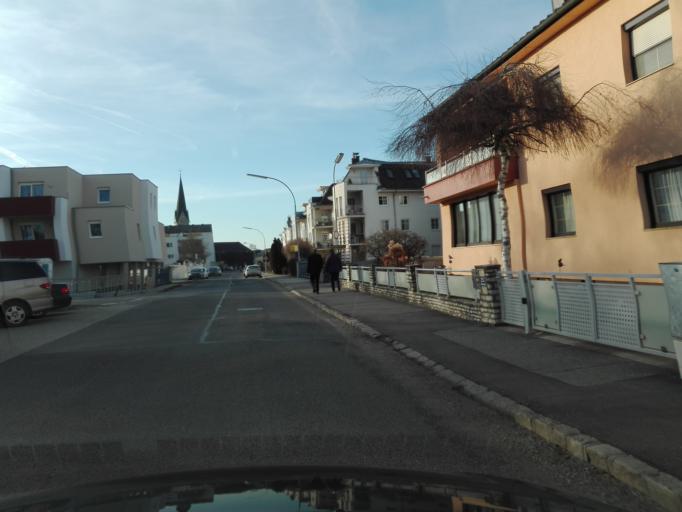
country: AT
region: Lower Austria
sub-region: Politischer Bezirk Amstetten
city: Sankt Valentin
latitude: 48.1742
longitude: 14.5376
